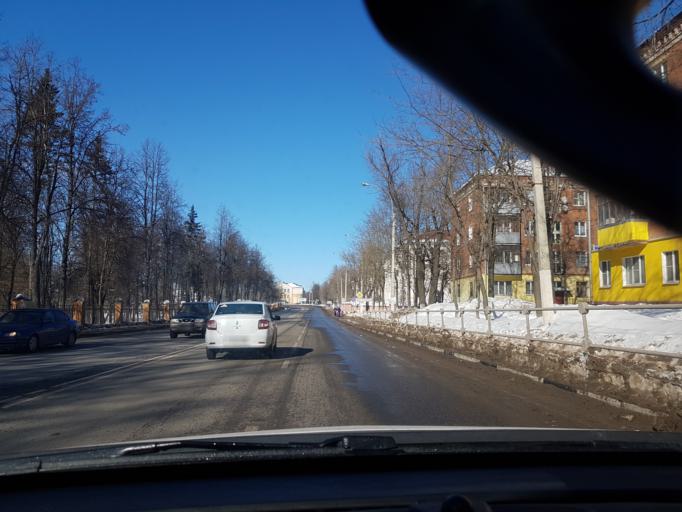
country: RU
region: Moskovskaya
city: Istra
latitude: 55.9173
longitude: 36.8585
